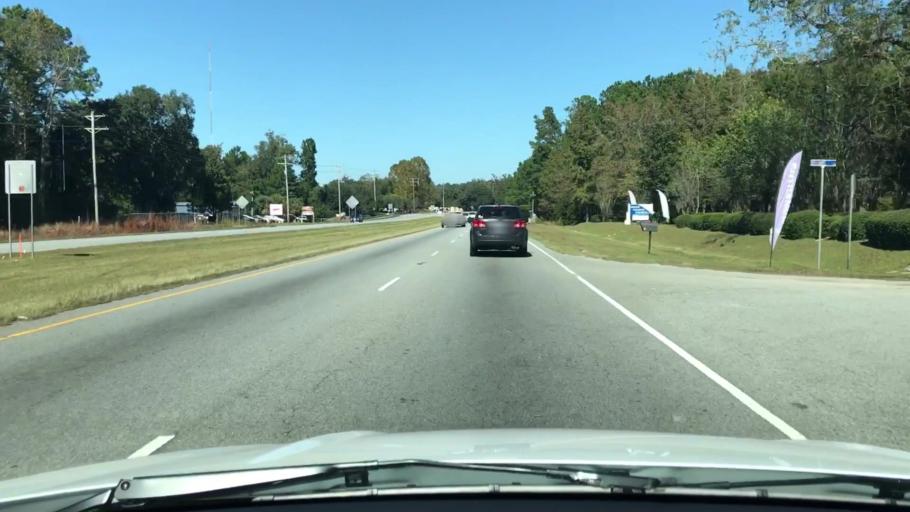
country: US
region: South Carolina
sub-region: Beaufort County
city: Bluffton
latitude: 32.3176
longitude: -80.9343
